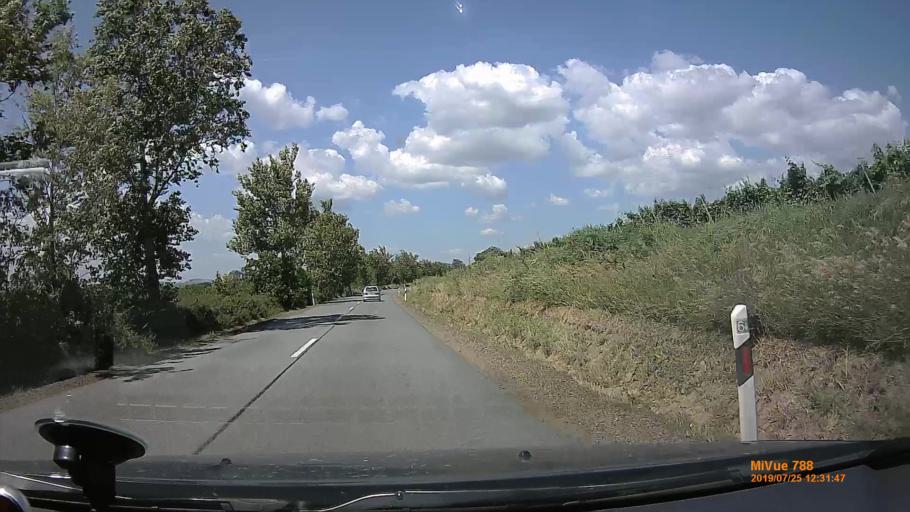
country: HU
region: Borsod-Abauj-Zemplen
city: Tarcal
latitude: 48.1453
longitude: 21.3237
